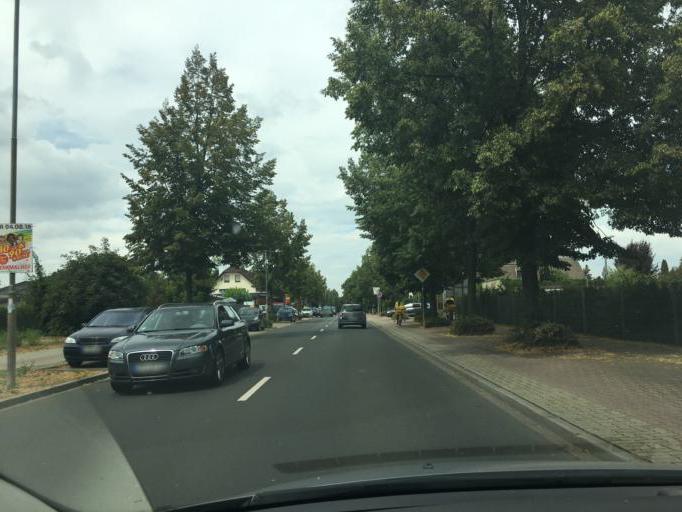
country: DE
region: Saxony-Anhalt
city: Merseburg
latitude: 51.3676
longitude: 11.9901
